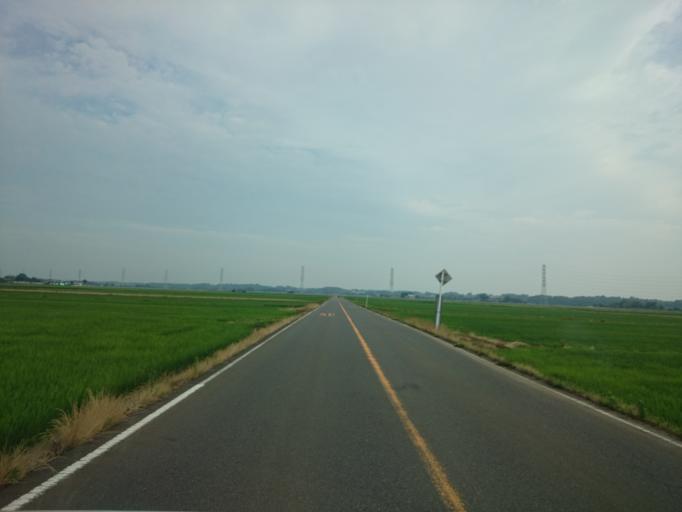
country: JP
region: Ibaraki
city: Tsukuba
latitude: 36.1630
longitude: 140.0990
